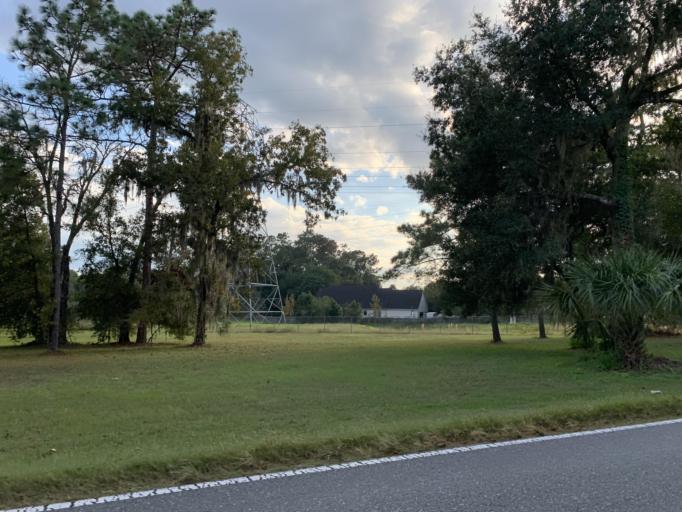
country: US
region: Florida
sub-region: Marion County
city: Silver Springs Shores
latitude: 29.1499
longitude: -82.0585
